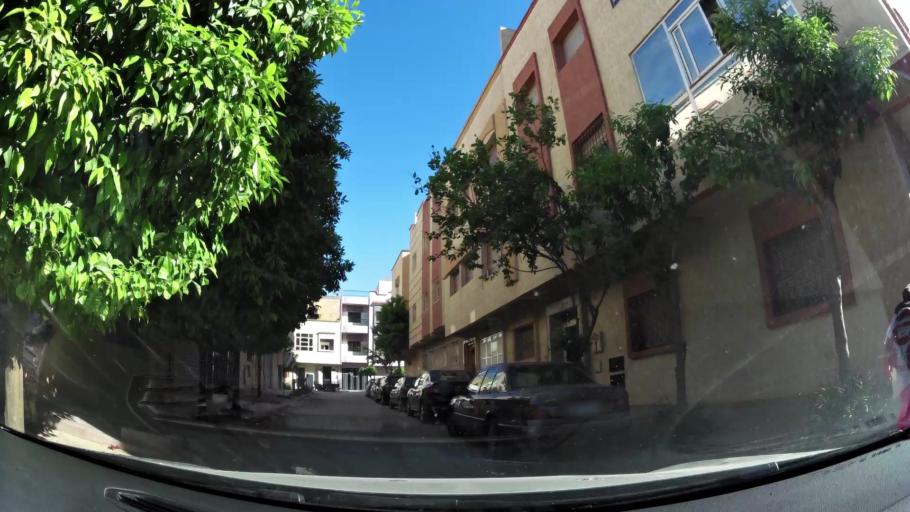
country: MA
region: Meknes-Tafilalet
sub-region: Meknes
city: Meknes
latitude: 33.8903
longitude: -5.5053
